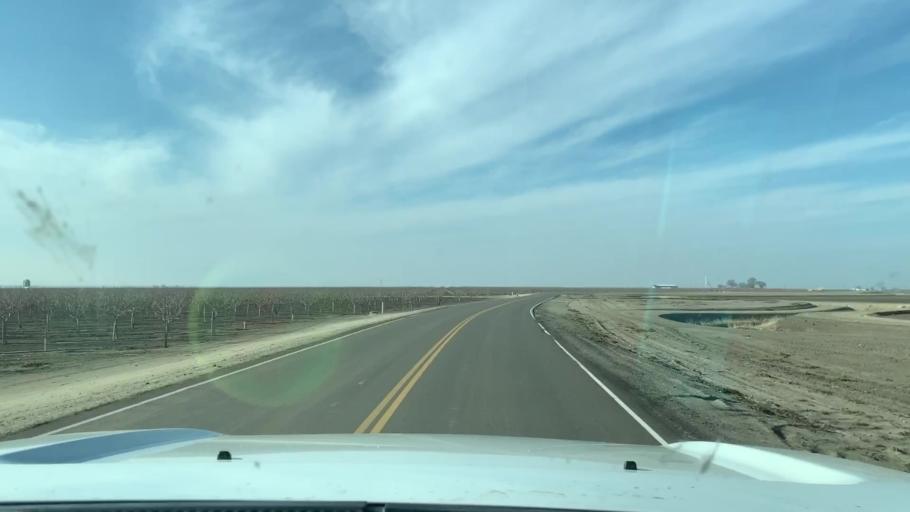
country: US
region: California
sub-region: Kern County
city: Buttonwillow
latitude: 35.4480
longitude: -119.5593
